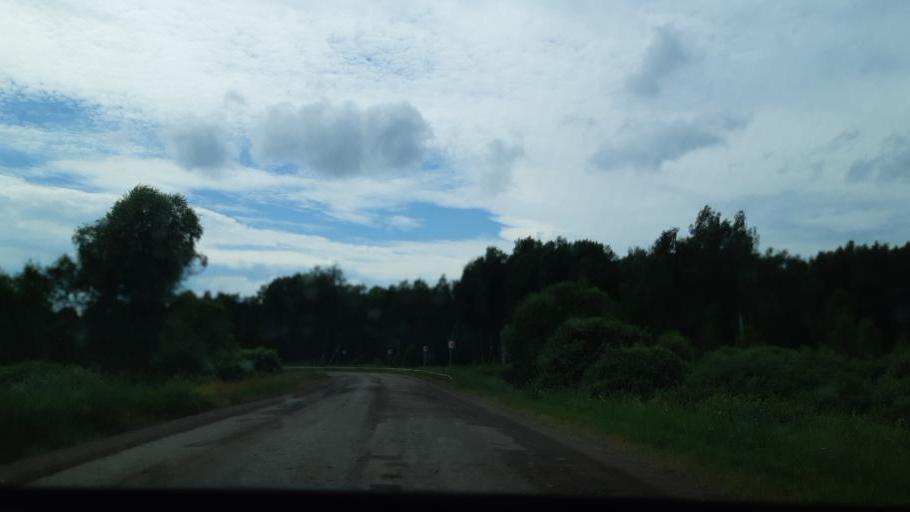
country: RU
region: Moskovskaya
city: Vereya
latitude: 55.3098
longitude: 36.1139
